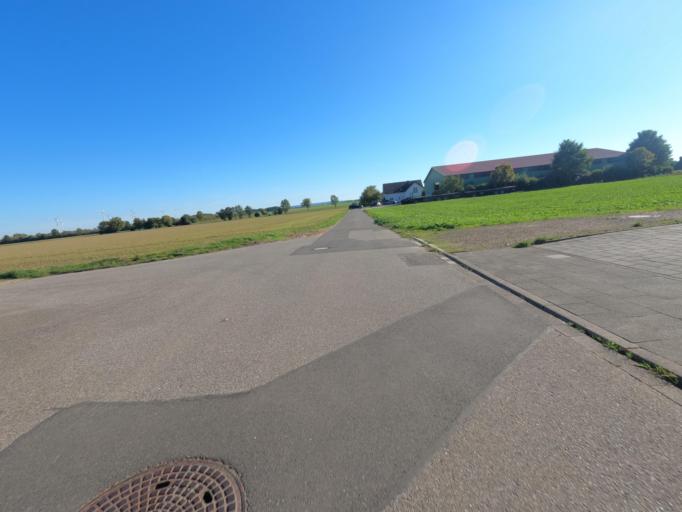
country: DE
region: North Rhine-Westphalia
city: Erkelenz
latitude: 51.0576
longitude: 6.3505
